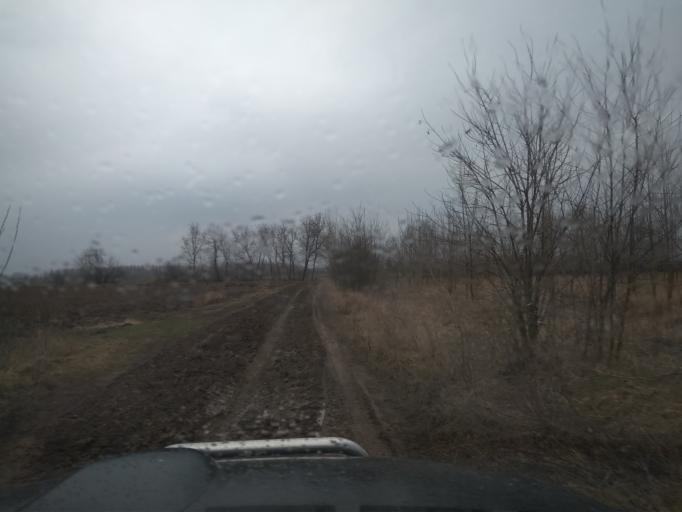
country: HU
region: Szabolcs-Szatmar-Bereg
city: Apagy
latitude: 47.9724
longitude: 21.9193
